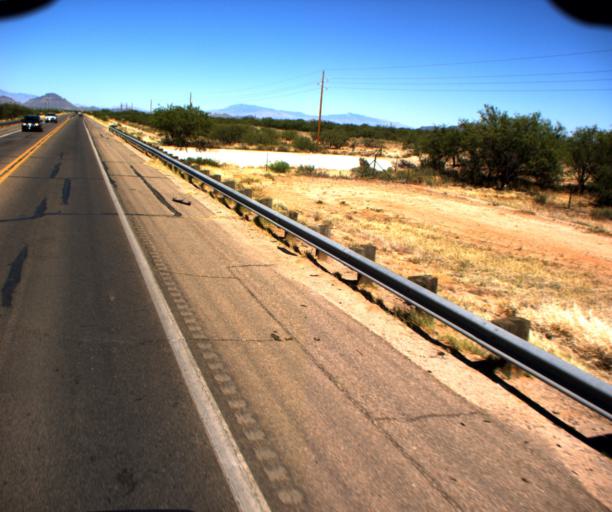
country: US
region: Arizona
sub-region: Pima County
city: Three Points
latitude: 32.1127
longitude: -111.2233
